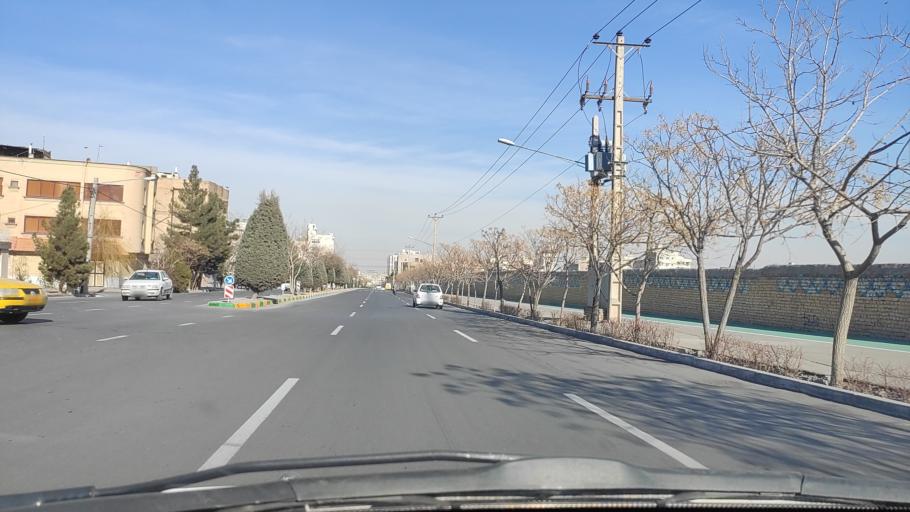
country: IR
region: Razavi Khorasan
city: Mashhad
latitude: 36.2865
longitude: 59.5326
